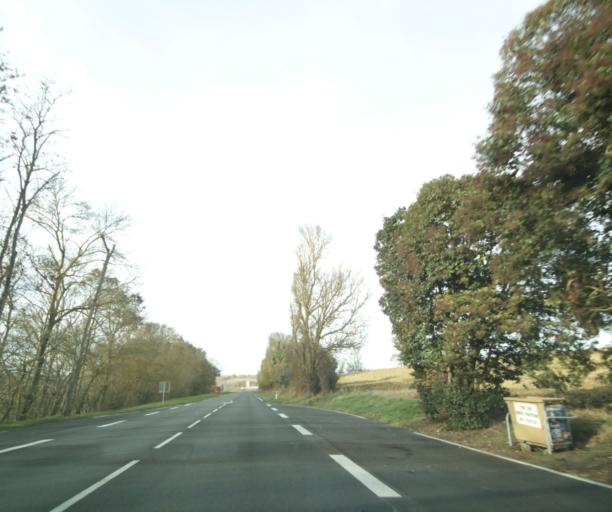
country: FR
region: Midi-Pyrenees
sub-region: Departement du Gers
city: Gimont
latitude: 43.6205
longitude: 0.9123
